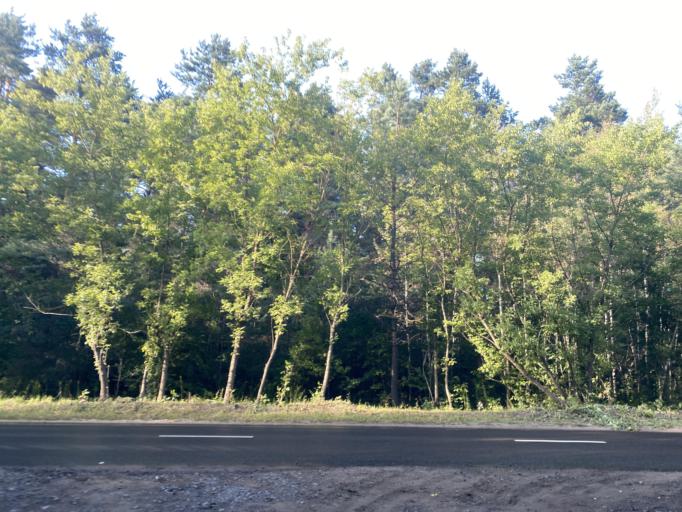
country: BY
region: Minsk
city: Vyaliki Trastsyanets
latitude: 53.9167
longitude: 27.6638
